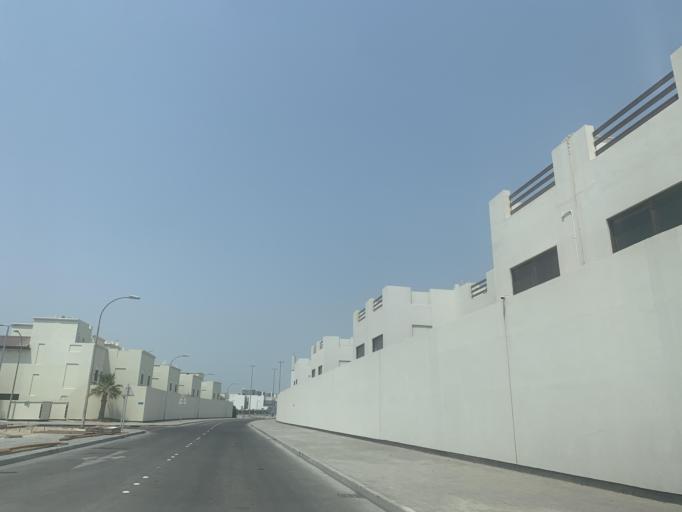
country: BH
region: Muharraq
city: Al Muharraq
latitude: 26.3102
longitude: 50.6277
